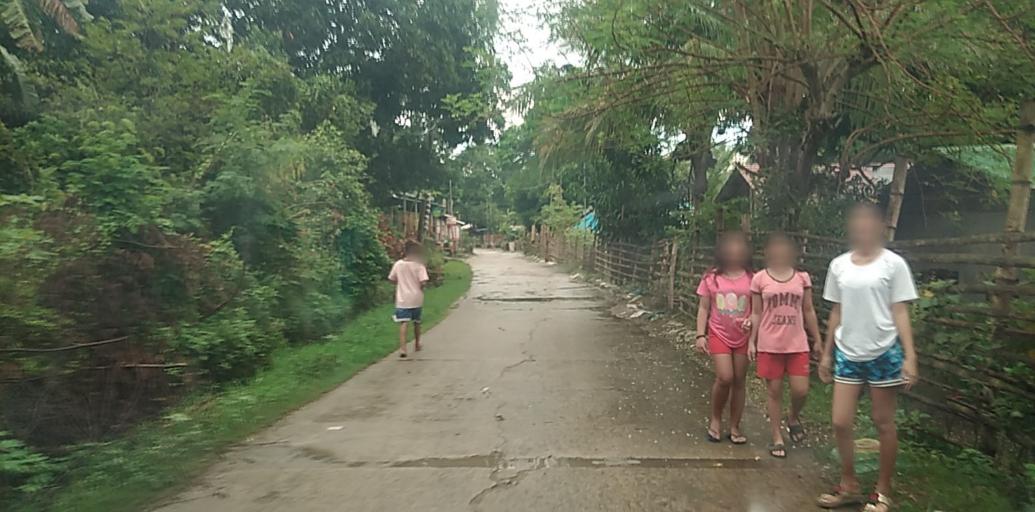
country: PH
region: Central Luzon
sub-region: Province of Pampanga
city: Arayat
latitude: 15.1534
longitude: 120.7423
